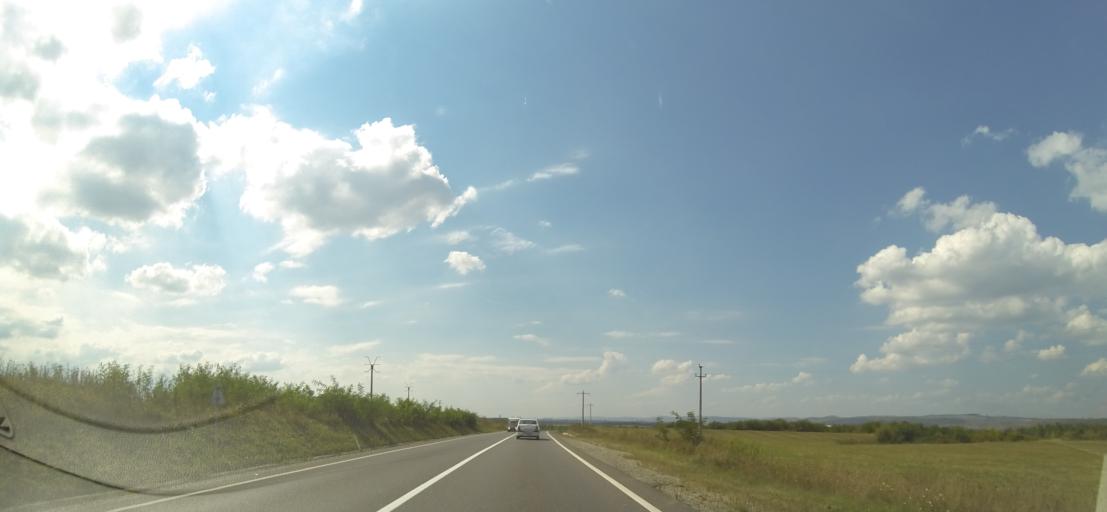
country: RO
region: Brasov
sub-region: Comuna Sercaia
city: Sercaia
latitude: 45.8248
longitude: 25.0996
